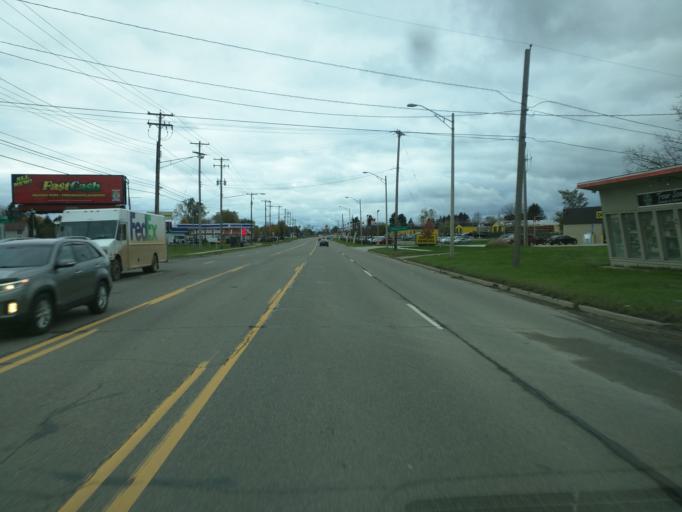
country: US
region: Michigan
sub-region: Ingham County
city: Edgemont Park
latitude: 42.7688
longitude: -84.5982
